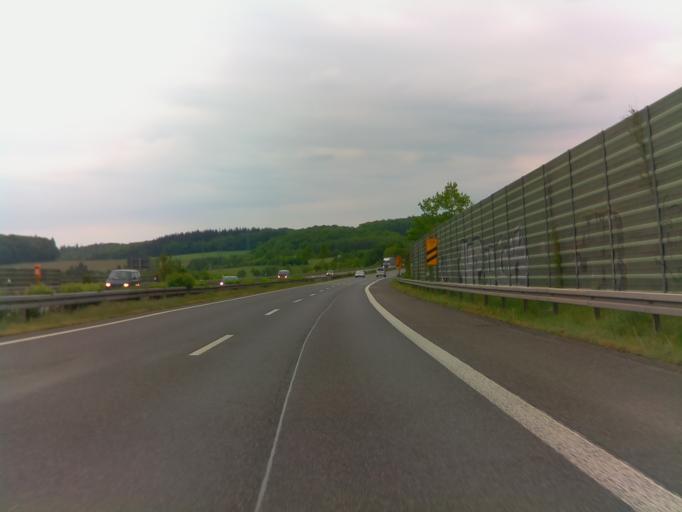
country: DE
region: Hesse
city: Staufenberg
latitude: 50.6605
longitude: 8.7211
